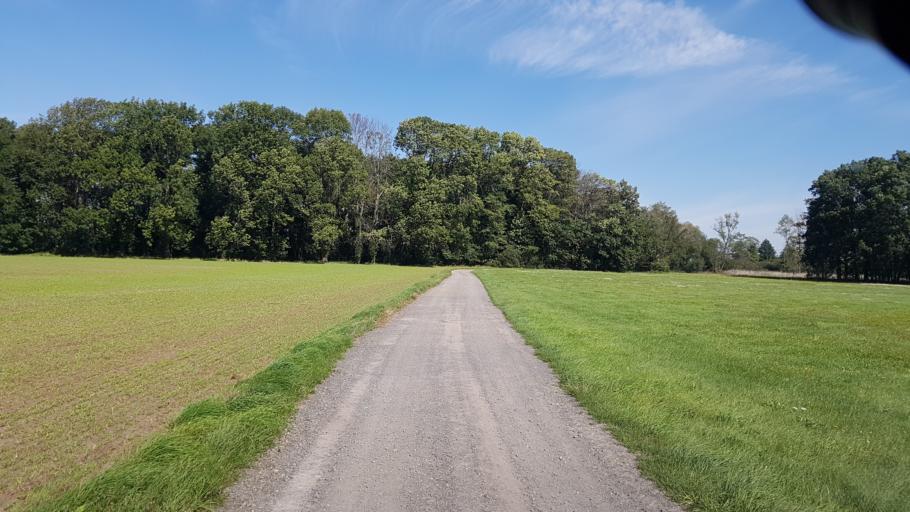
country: DE
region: Brandenburg
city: Sonnewalde
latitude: 51.6703
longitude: 13.6717
